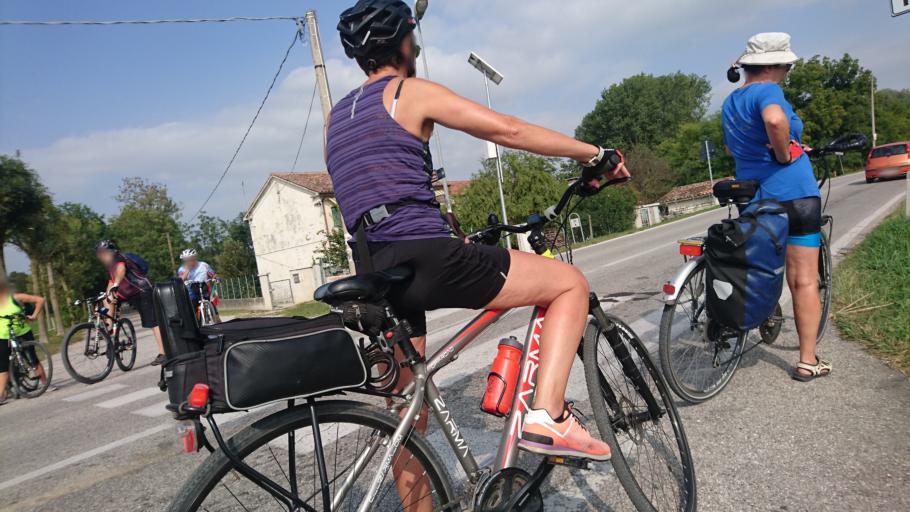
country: IT
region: Veneto
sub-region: Provincia di Padova
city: Grantorto
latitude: 45.5889
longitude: 11.7584
